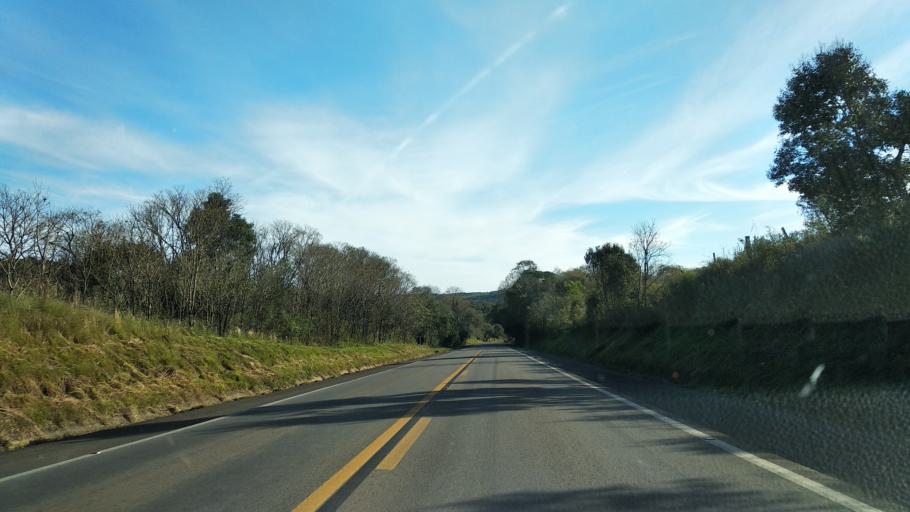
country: BR
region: Santa Catarina
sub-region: Celso Ramos
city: Celso Ramos
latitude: -27.5475
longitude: -51.4334
